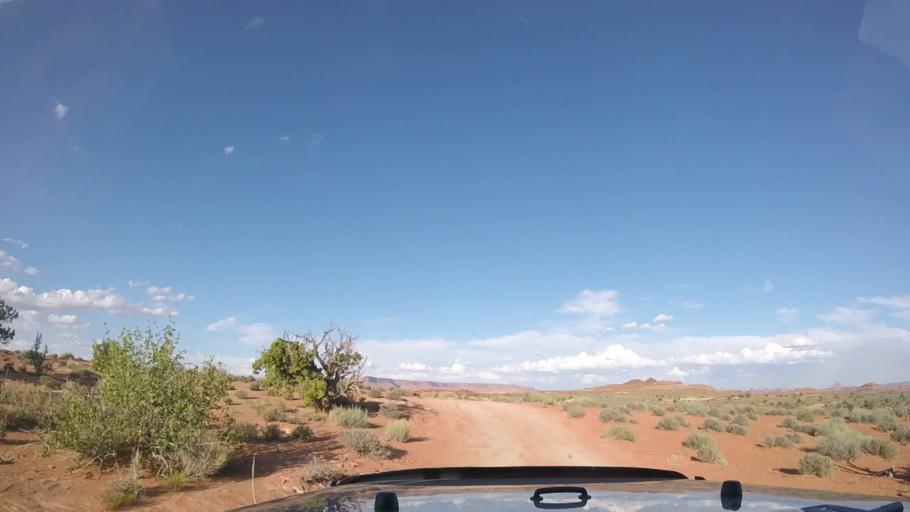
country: US
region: Utah
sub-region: Grand County
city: Moab
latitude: 38.2161
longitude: -109.7999
